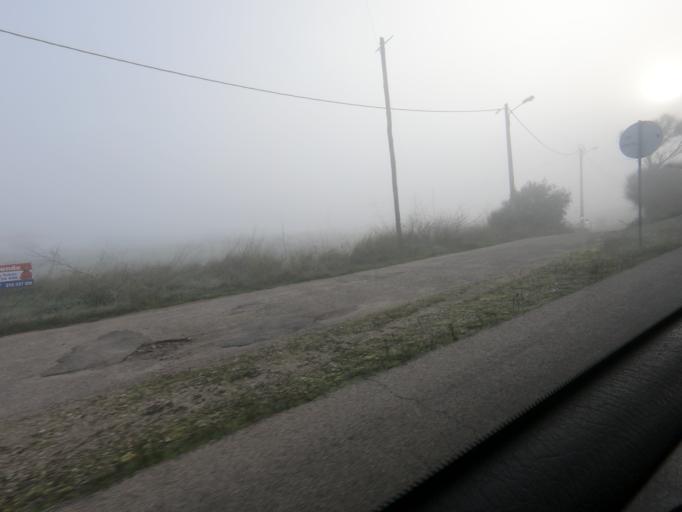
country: PT
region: Setubal
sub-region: Palmela
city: Palmela
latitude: 38.5883
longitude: -8.8367
